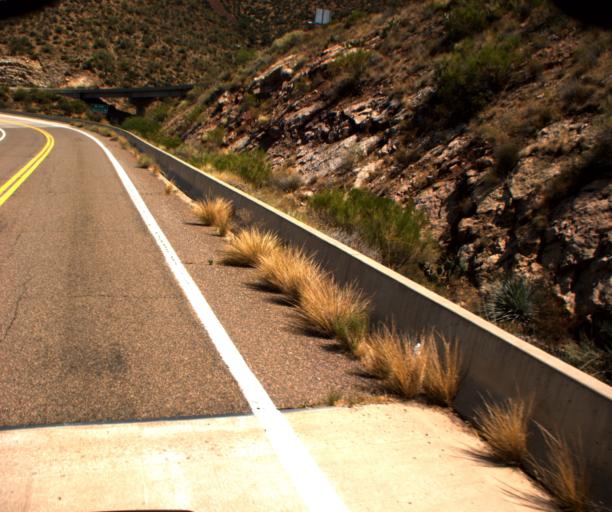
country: US
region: Arizona
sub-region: Gila County
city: Tonto Basin
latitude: 33.6728
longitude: -111.1552
